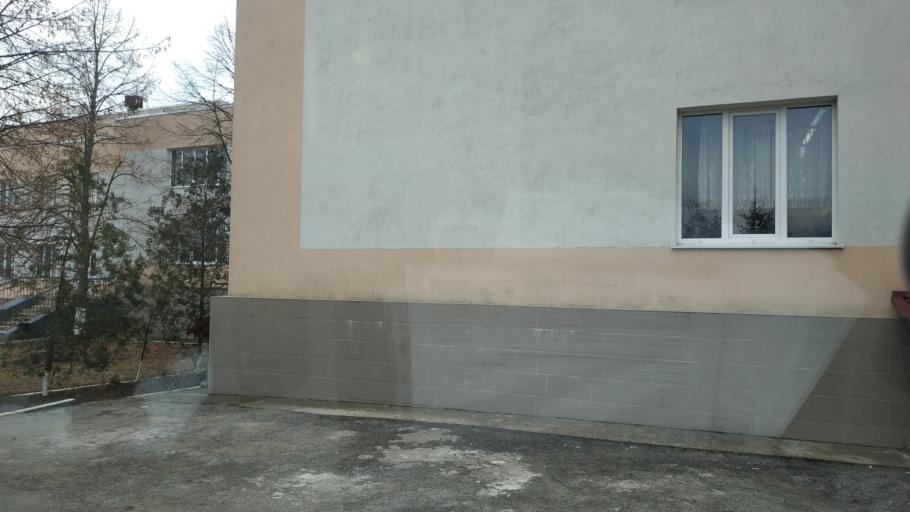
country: MD
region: Anenii Noi
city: Varnita
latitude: 46.8404
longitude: 29.3580
